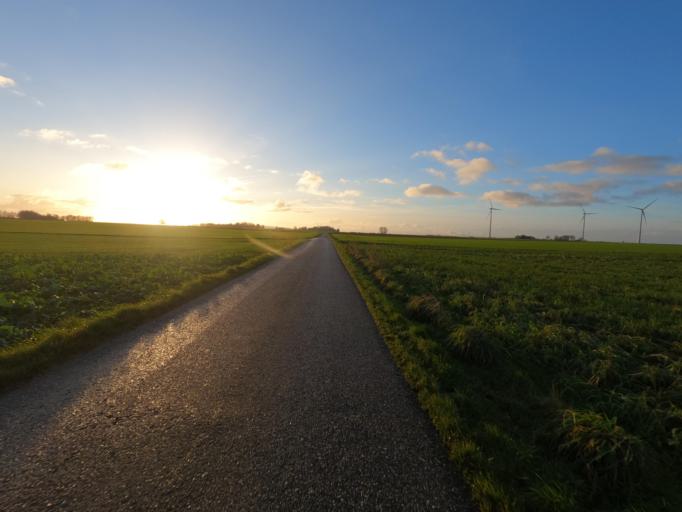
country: DE
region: North Rhine-Westphalia
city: Erkelenz
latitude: 51.0274
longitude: 6.3592
